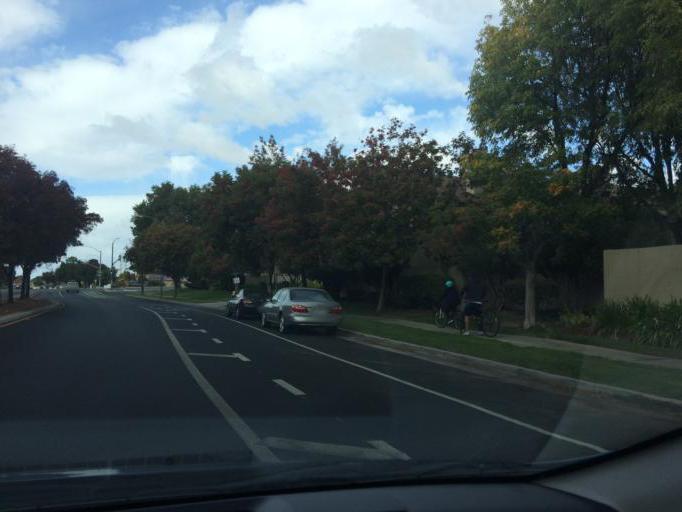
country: US
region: California
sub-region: Santa Clara County
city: Seven Trees
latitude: 37.3113
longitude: -121.8011
